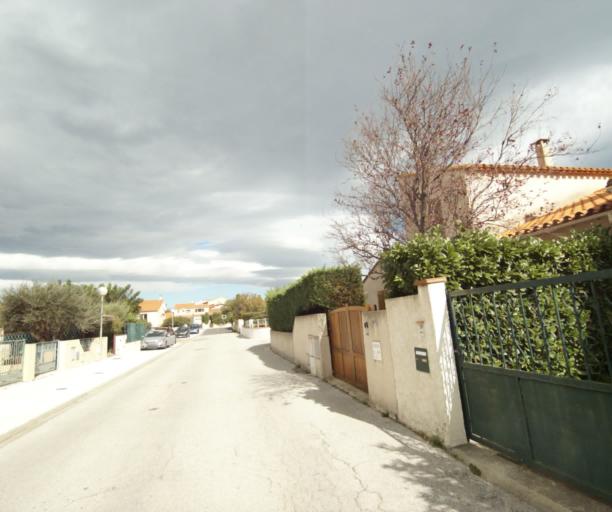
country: FR
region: Languedoc-Roussillon
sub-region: Departement des Pyrenees-Orientales
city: Argelers
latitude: 42.5522
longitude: 3.0177
